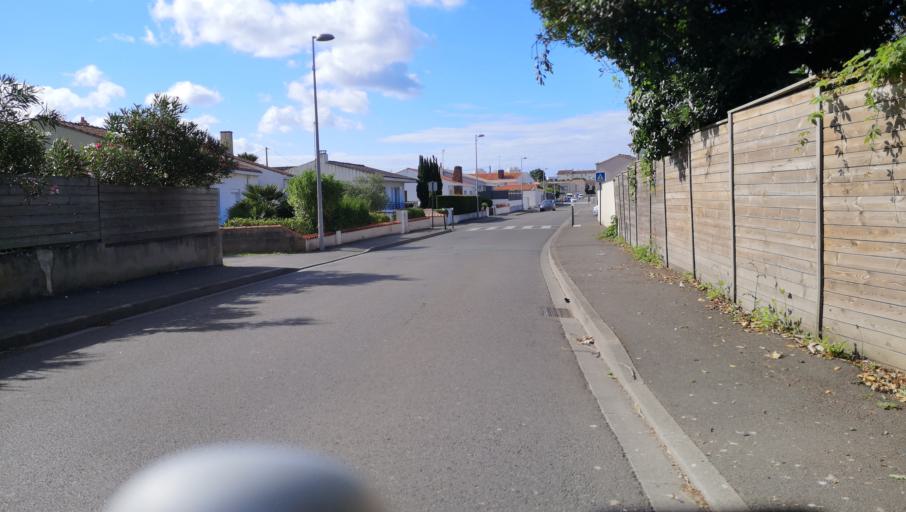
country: FR
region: Pays de la Loire
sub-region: Departement de la Vendee
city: Les Sables-d'Olonne
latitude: 46.5033
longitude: -1.7733
